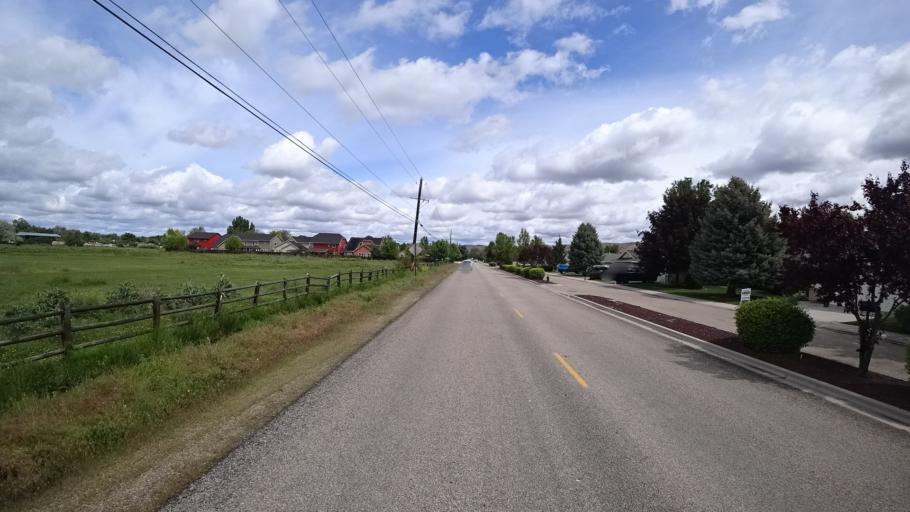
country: US
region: Idaho
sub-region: Ada County
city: Eagle
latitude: 43.6793
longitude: -116.3016
